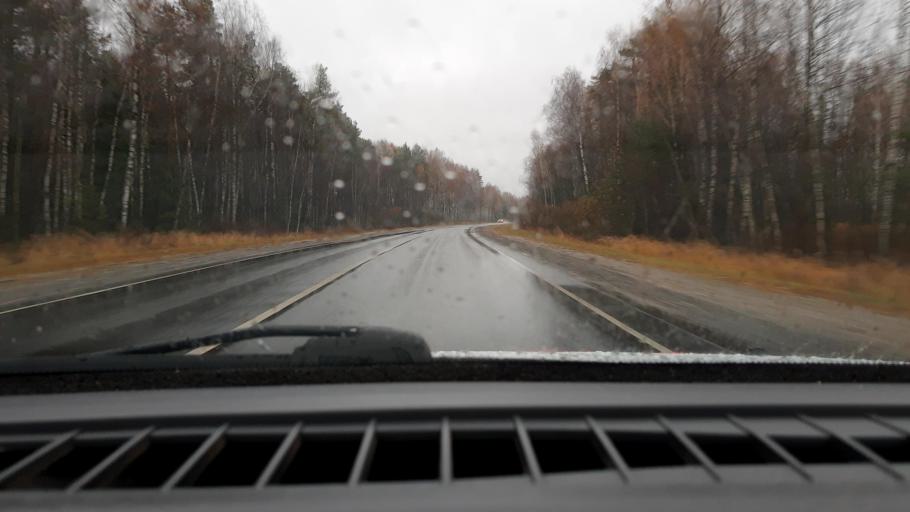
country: RU
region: Nizjnij Novgorod
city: Linda
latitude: 56.6472
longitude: 44.1144
